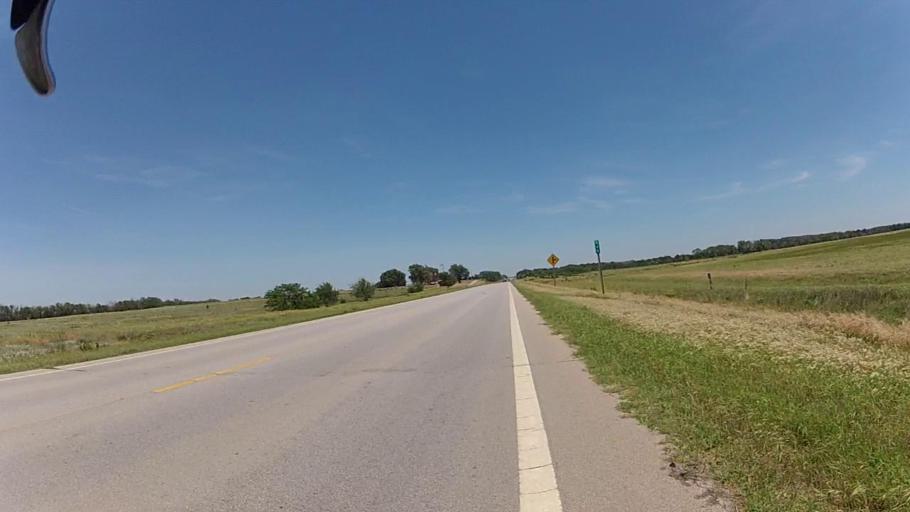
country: US
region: Kansas
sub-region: Harper County
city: Harper
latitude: 37.2391
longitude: -98.1713
